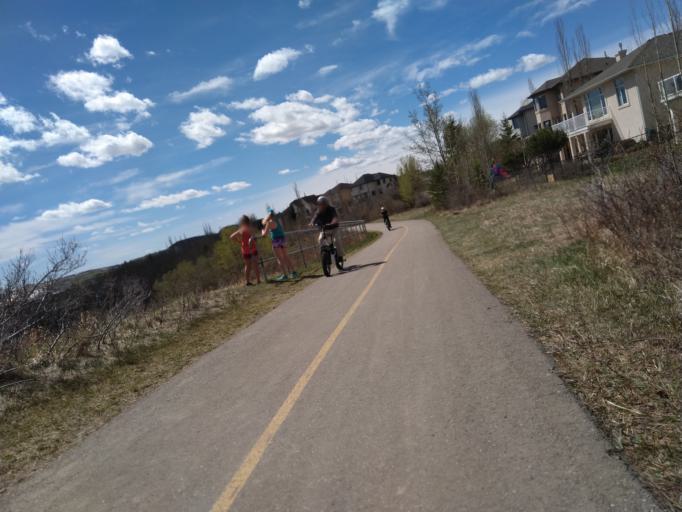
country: CA
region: Alberta
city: Calgary
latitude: 51.1231
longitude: -114.2373
